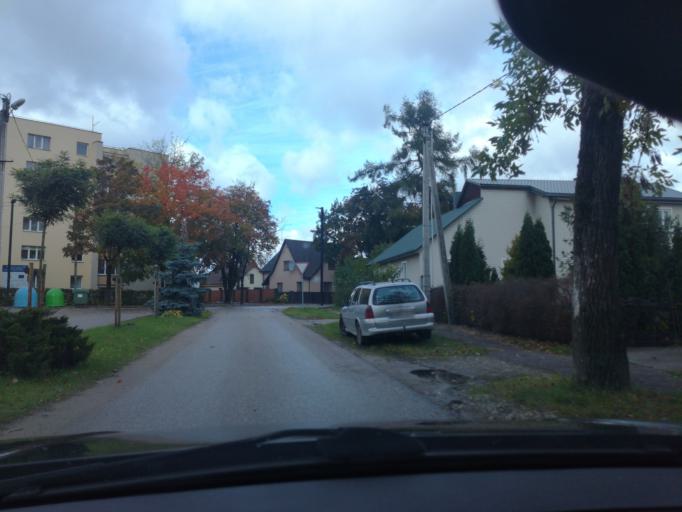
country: LT
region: Alytaus apskritis
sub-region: Alytus
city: Alytus
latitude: 54.3908
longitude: 24.0447
